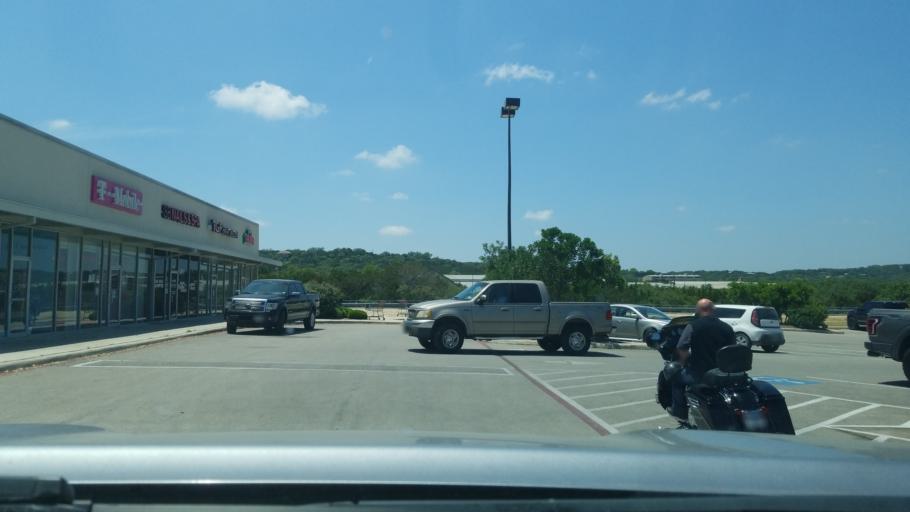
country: US
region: Texas
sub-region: Comal County
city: Bulverde
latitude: 29.7966
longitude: -98.4308
